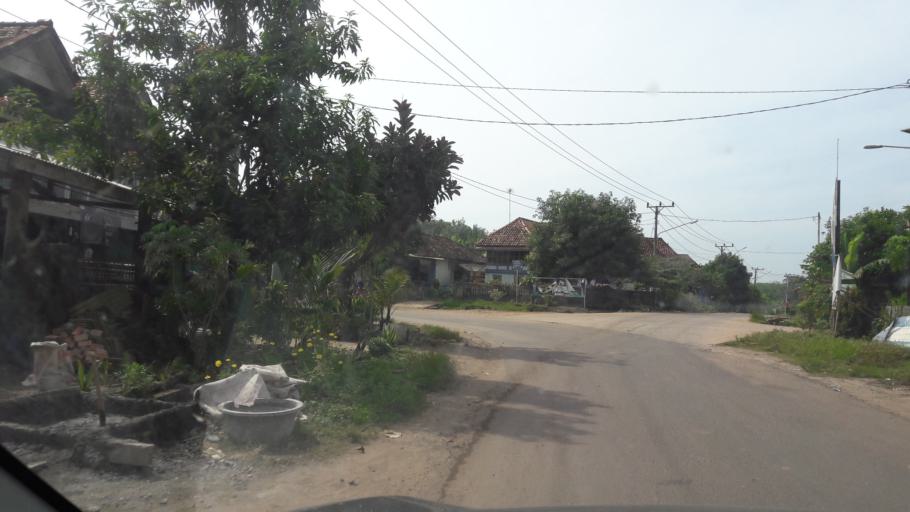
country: ID
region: South Sumatra
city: Gunungmenang
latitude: -3.3117
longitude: 104.1130
